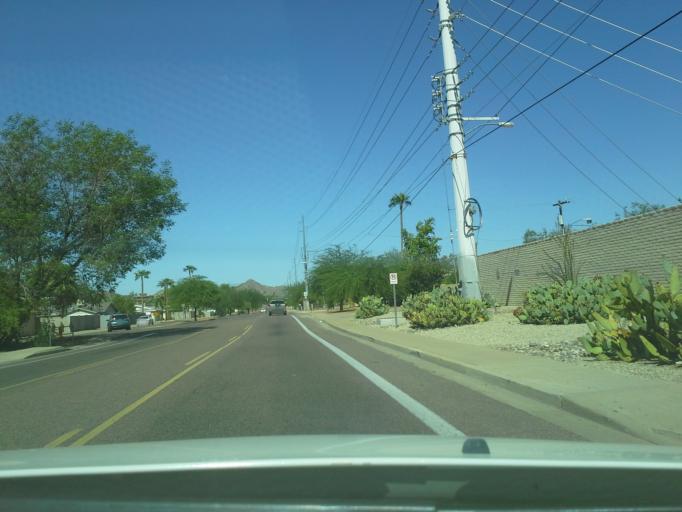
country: US
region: Arizona
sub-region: Maricopa County
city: Phoenix
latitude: 33.5563
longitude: -112.0566
